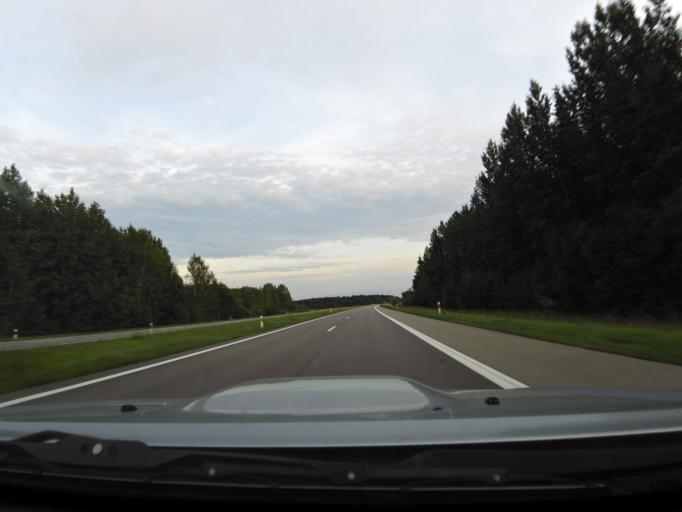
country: LT
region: Vilnius County
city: Ukmerge
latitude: 55.5129
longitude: 24.6028
